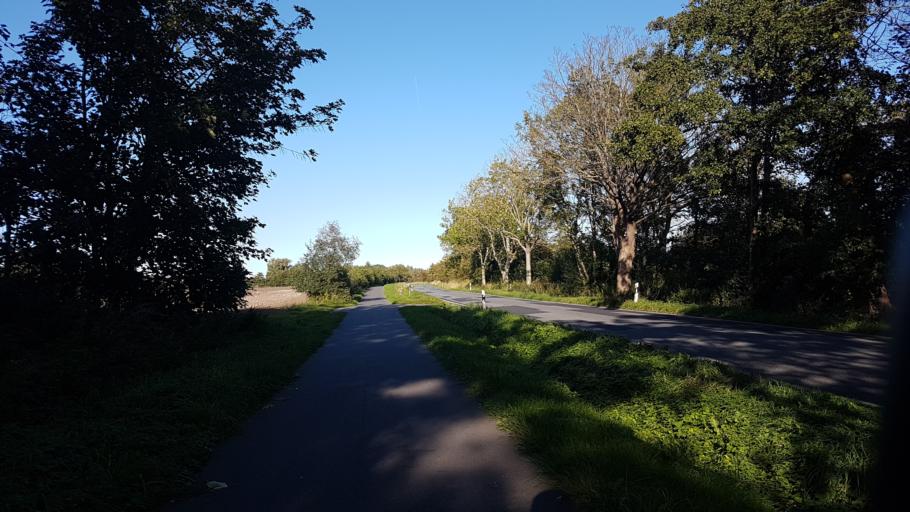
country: DE
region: Mecklenburg-Vorpommern
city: Dranske
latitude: 54.6408
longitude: 13.2569
